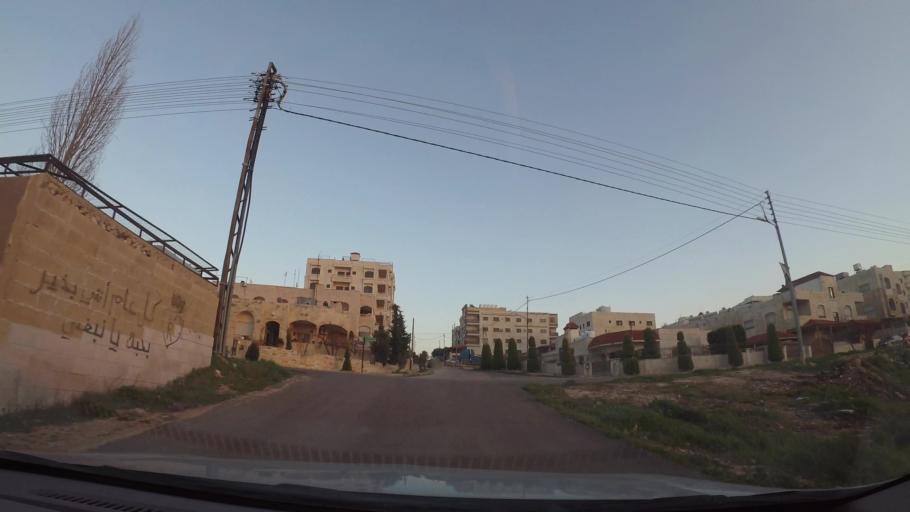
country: JO
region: Amman
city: Al Quwaysimah
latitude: 31.8982
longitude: 35.9268
